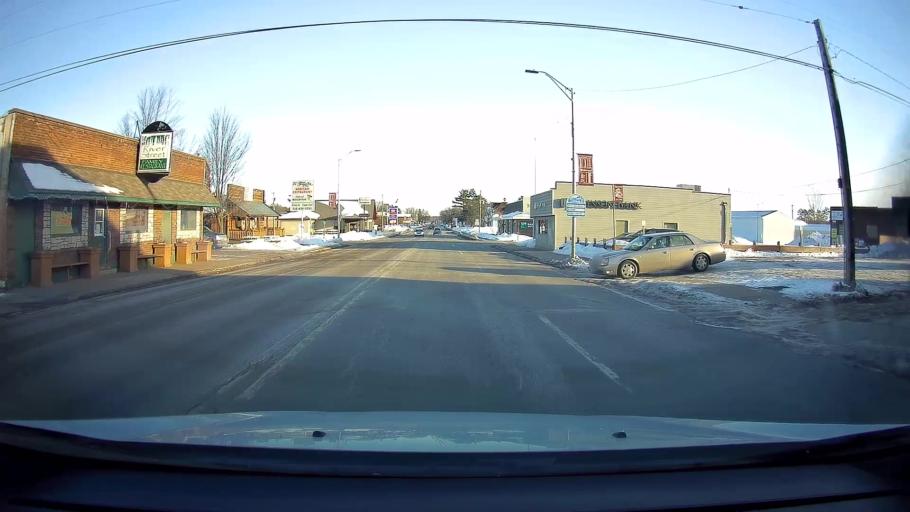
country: US
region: Wisconsin
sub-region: Washburn County
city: Spooner
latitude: 45.8271
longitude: -91.8880
